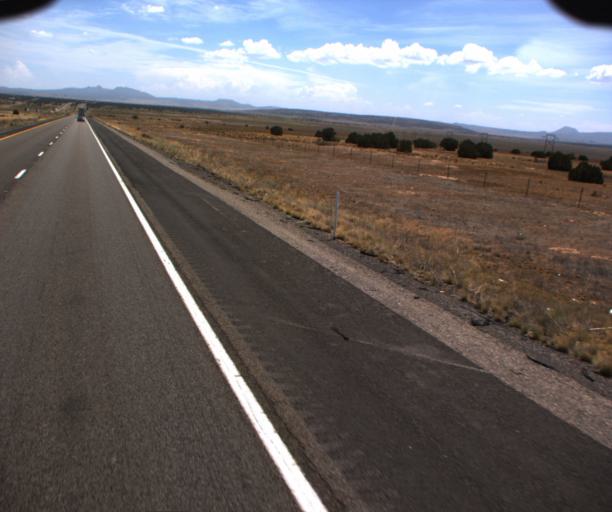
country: US
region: Arizona
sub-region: Mohave County
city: Peach Springs
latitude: 35.3051
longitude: -112.9931
